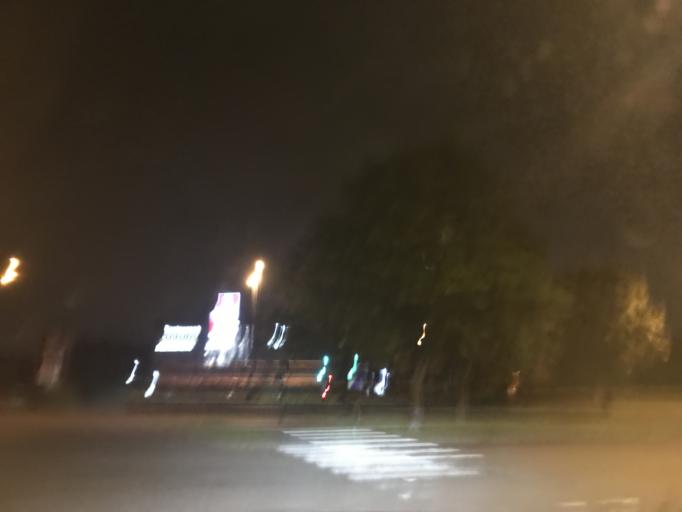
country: FR
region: Ile-de-France
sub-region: Departement des Yvelines
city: Sartrouville
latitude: 48.9484
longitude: 2.1987
